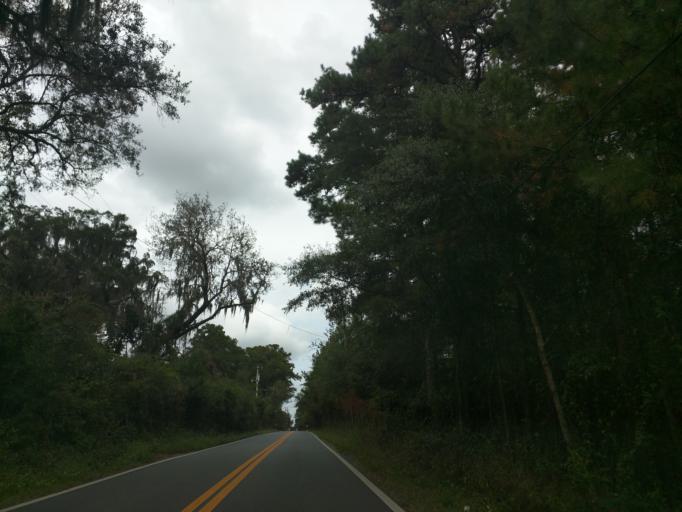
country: US
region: Florida
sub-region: Leon County
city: Tallahassee
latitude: 30.4116
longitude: -84.2100
